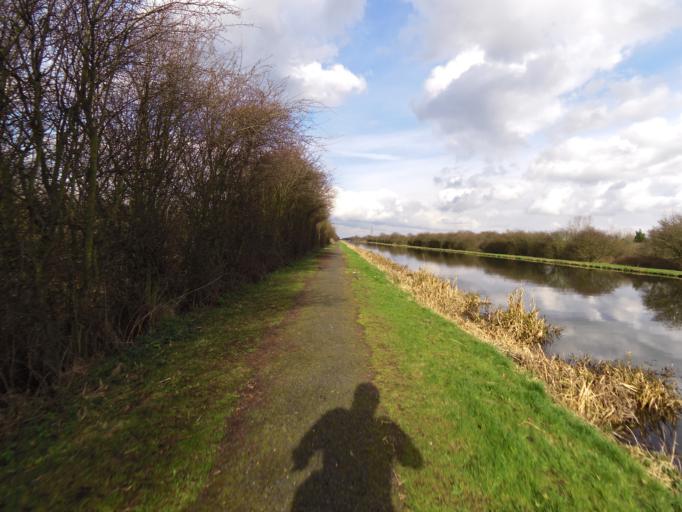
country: GB
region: England
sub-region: Doncaster
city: Stainforth
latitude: 53.6252
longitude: -1.0466
